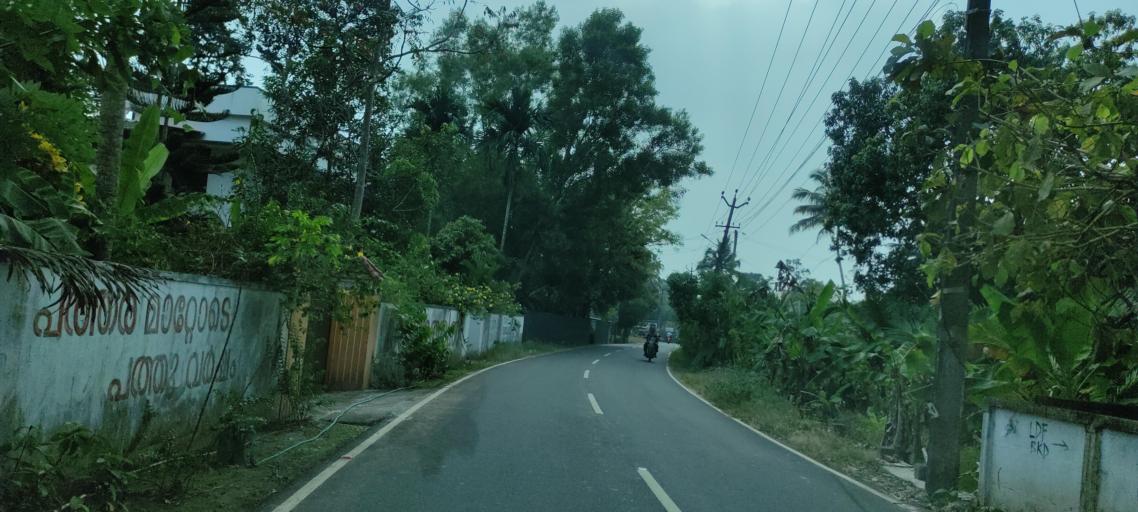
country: IN
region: Kerala
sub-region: Alappuzha
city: Shertallai
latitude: 9.5984
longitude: 76.3410
